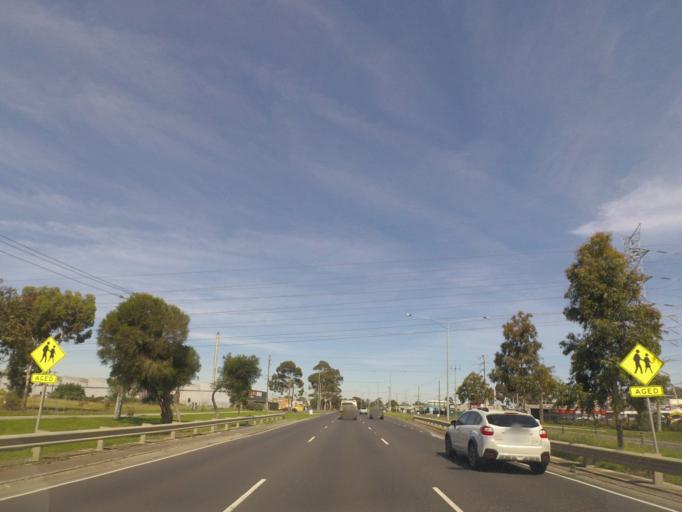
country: AU
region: Victoria
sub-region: Brimbank
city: Sunshine North
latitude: -37.7752
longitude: 144.8125
